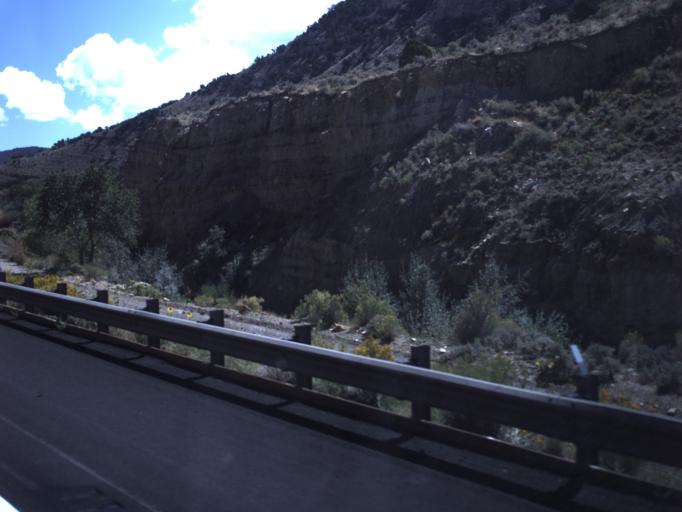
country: US
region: Utah
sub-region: Sevier County
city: Salina
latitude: 38.9039
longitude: -111.6830
